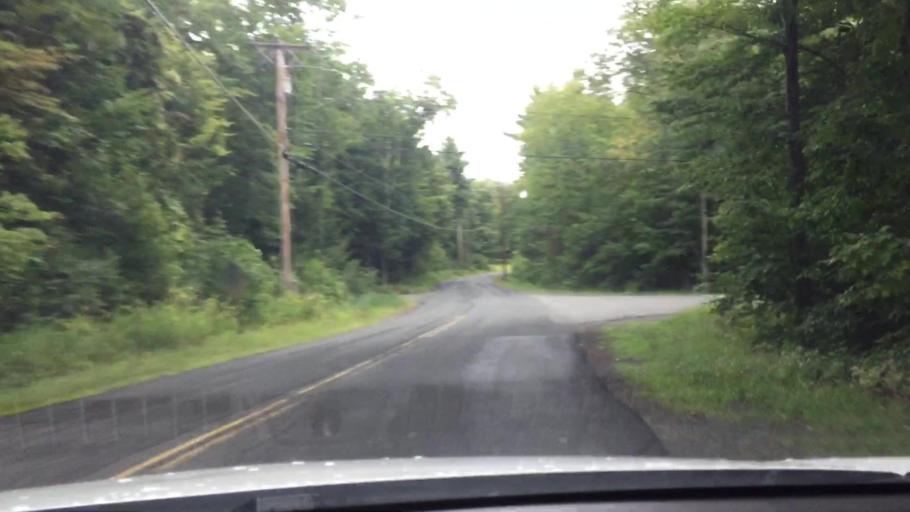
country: US
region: Massachusetts
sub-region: Berkshire County
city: Otis
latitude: 42.1714
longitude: -73.0539
